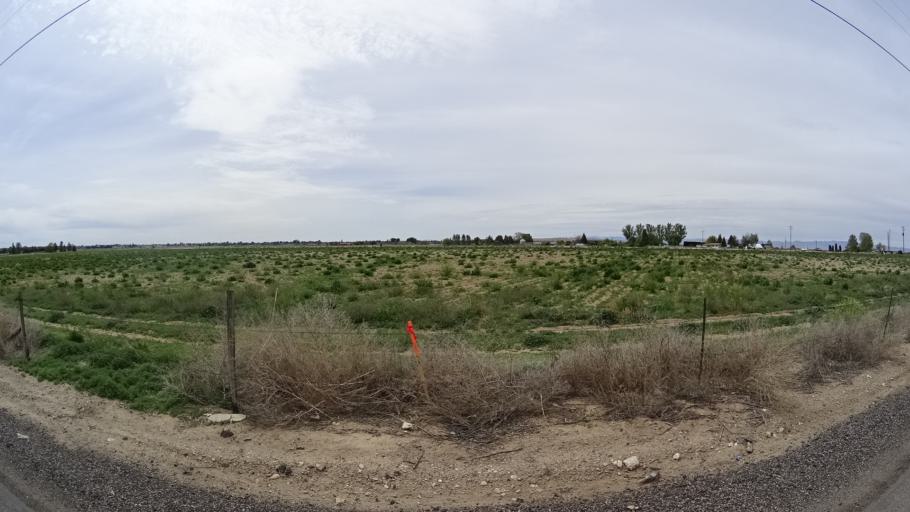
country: US
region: Idaho
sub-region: Ada County
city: Kuna
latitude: 43.5321
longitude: -116.4119
